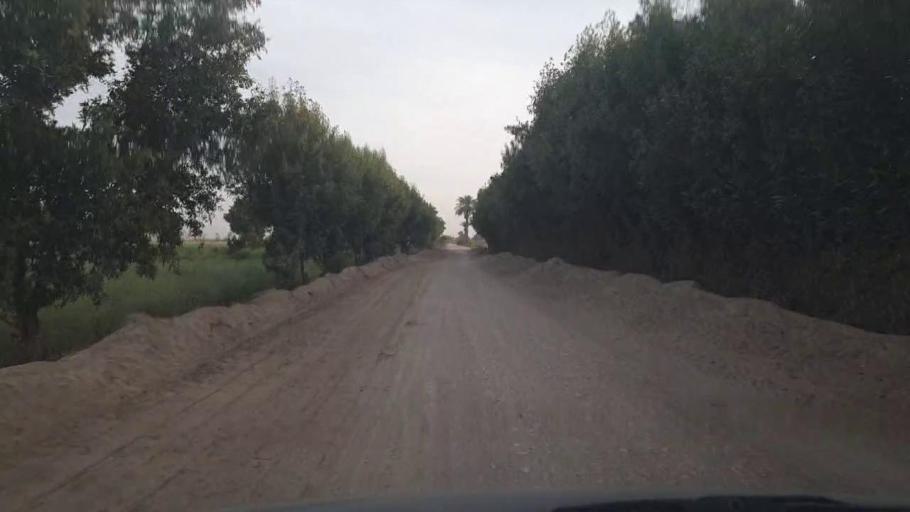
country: PK
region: Sindh
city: Kunri
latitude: 25.2253
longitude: 69.5741
